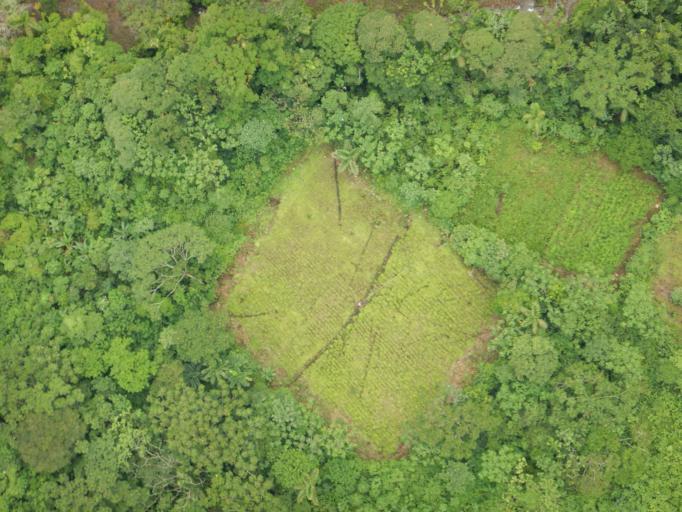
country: BO
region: Cochabamba
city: Chimore
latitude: -17.1663
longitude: -65.2570
